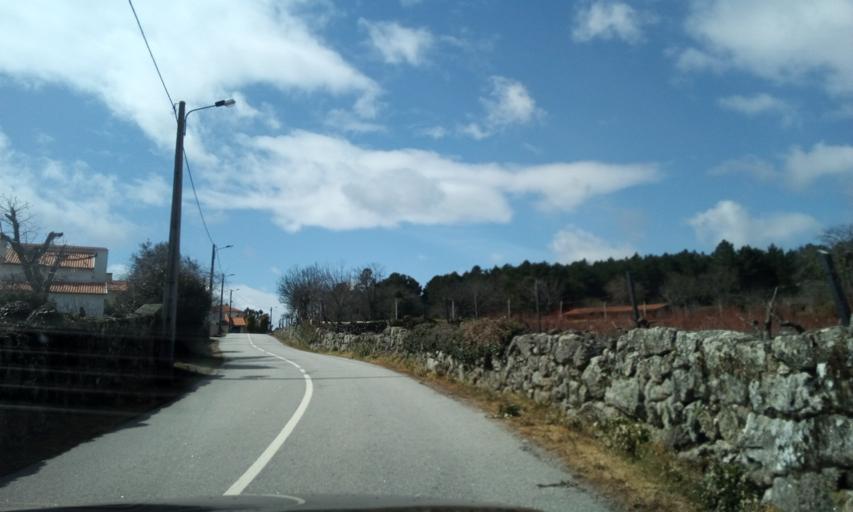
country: PT
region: Guarda
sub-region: Fornos de Algodres
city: Fornos de Algodres
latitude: 40.6308
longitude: -7.5397
